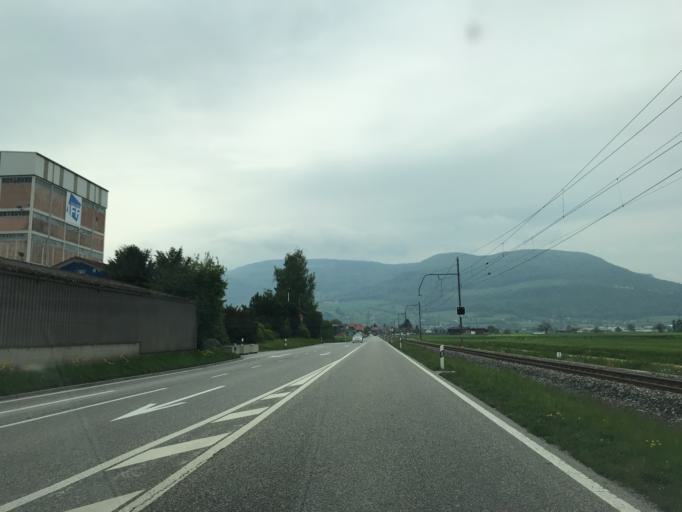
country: CH
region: Bern
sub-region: Oberaargau
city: Niederbipp
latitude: 47.2550
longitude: 7.7156
